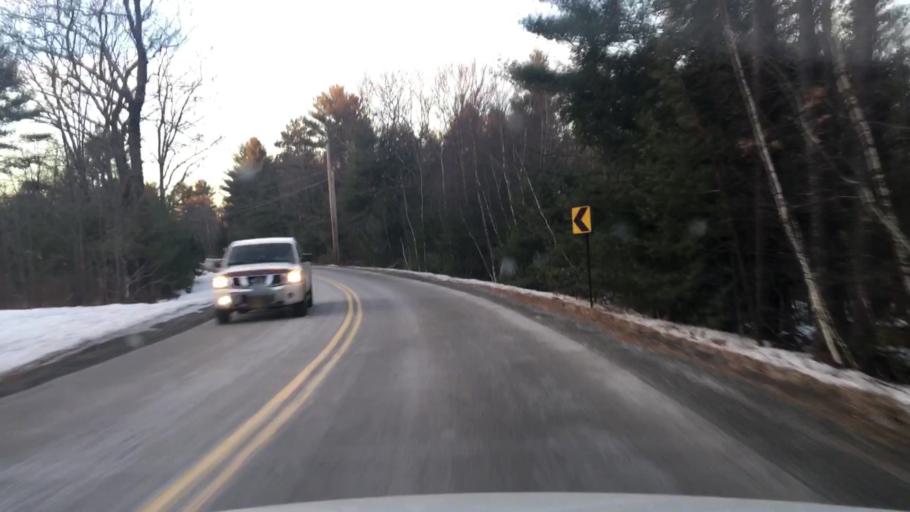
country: US
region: Maine
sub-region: York County
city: Lebanon
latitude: 43.3380
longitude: -70.8641
